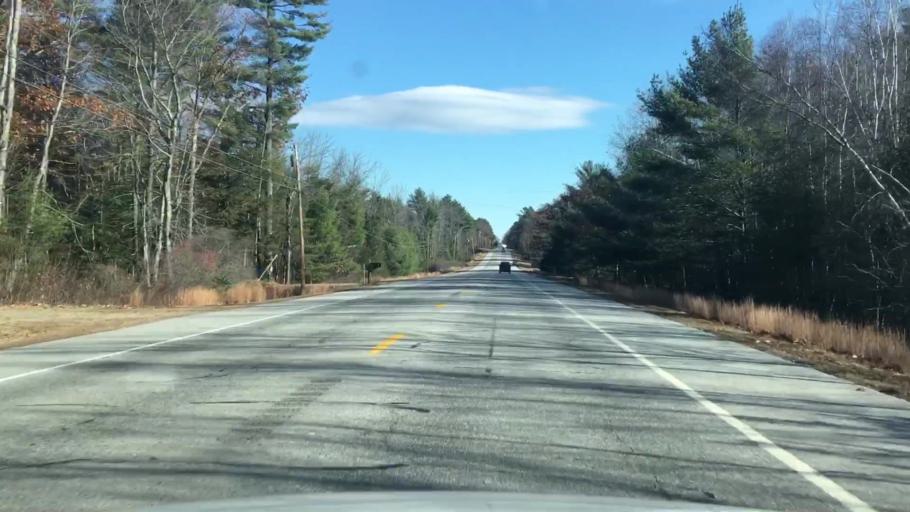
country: US
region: Maine
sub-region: Kennebec County
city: Windsor
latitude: 44.2782
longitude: -69.6195
